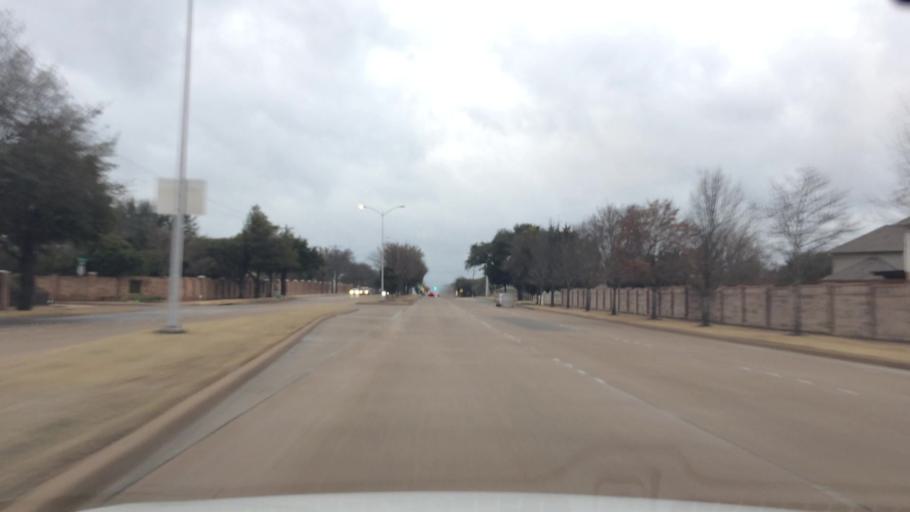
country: US
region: Texas
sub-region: Collin County
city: Frisco
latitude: 33.0975
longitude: -96.7716
